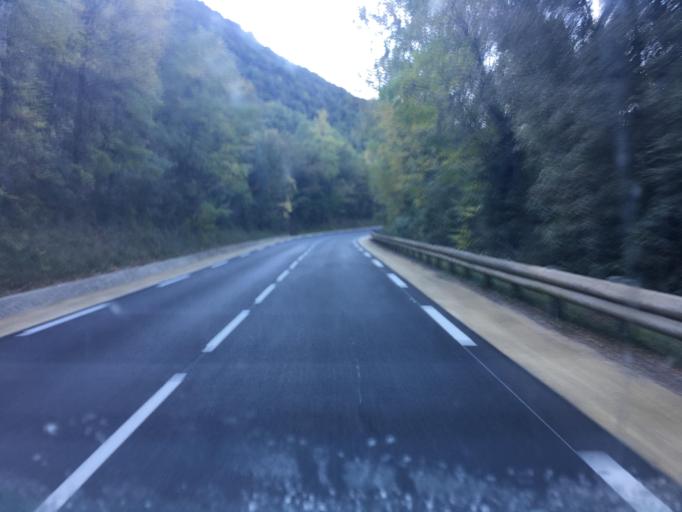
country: FR
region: Languedoc-Roussillon
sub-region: Departement de l'Herault
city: Ganges
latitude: 43.9559
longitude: 3.6869
